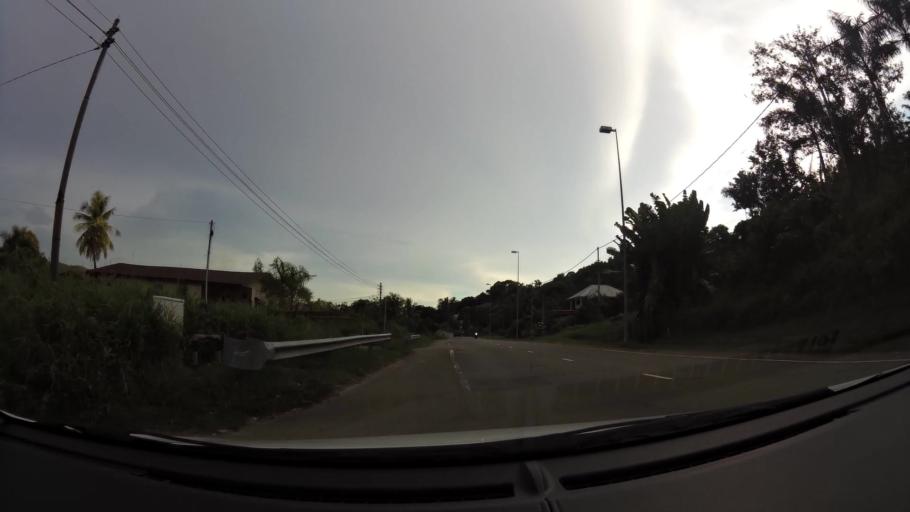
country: BN
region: Brunei and Muara
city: Bandar Seri Begawan
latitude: 4.9032
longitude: 114.9917
